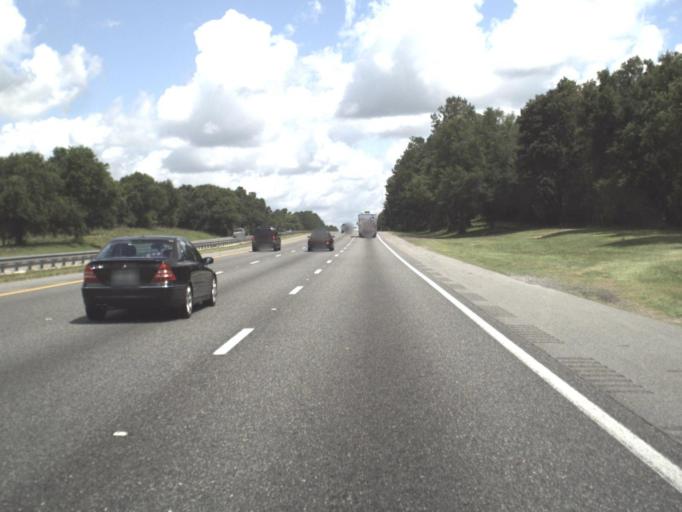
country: US
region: Florida
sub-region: Columbia County
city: Lake City
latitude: 30.0915
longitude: -82.6405
